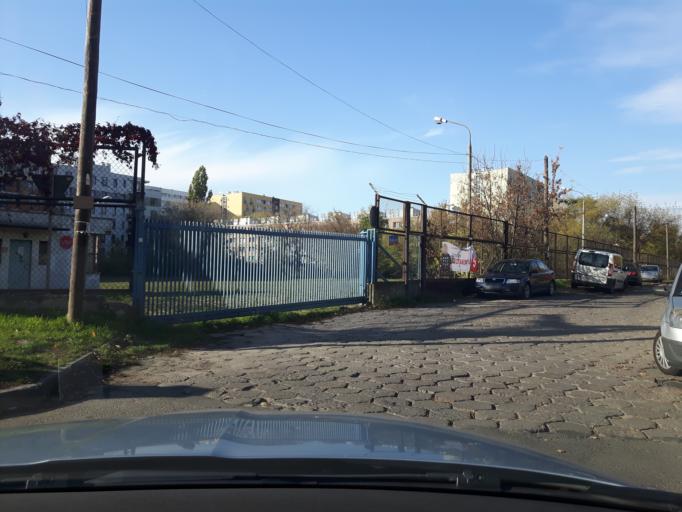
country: PL
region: Masovian Voivodeship
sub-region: Warszawa
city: Bemowo
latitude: 52.2303
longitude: 20.9377
